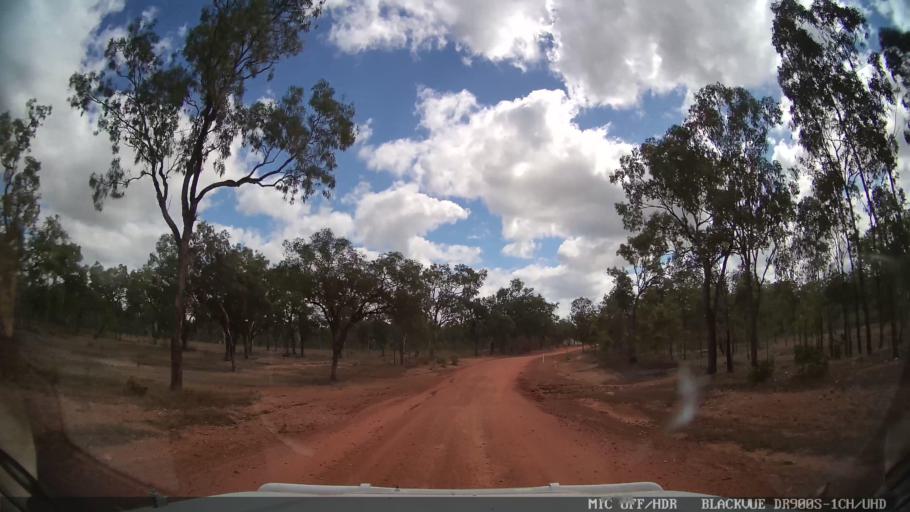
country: AU
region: Queensland
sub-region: Cook
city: Cooktown
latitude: -15.3523
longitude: 144.4604
